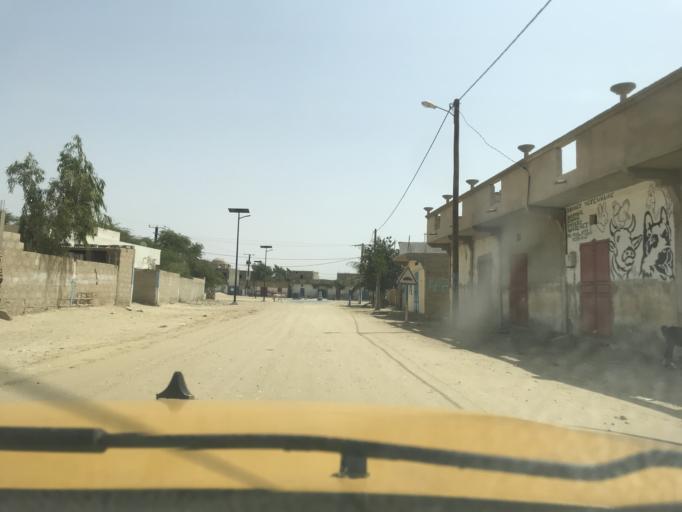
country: SN
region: Saint-Louis
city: Saint-Louis
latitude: 16.0201
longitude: -16.4467
